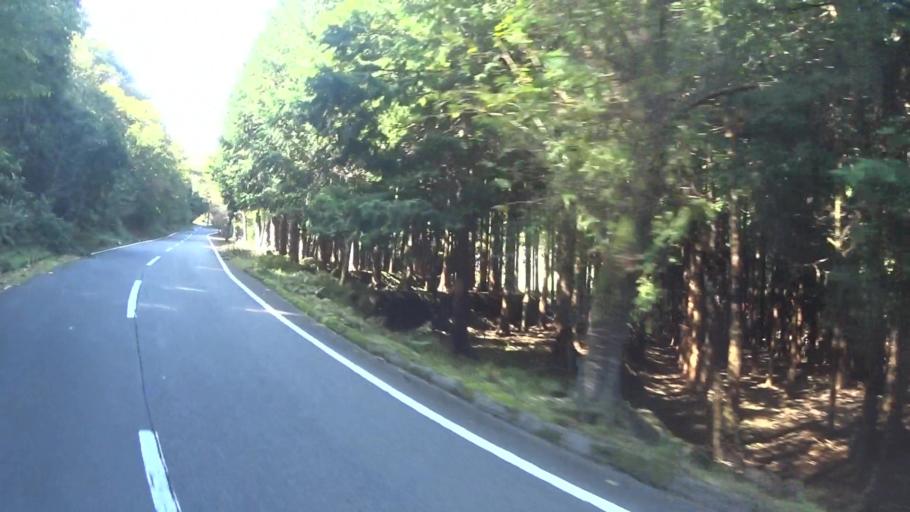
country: JP
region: Hyogo
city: Toyooka
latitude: 35.5350
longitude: 134.9257
